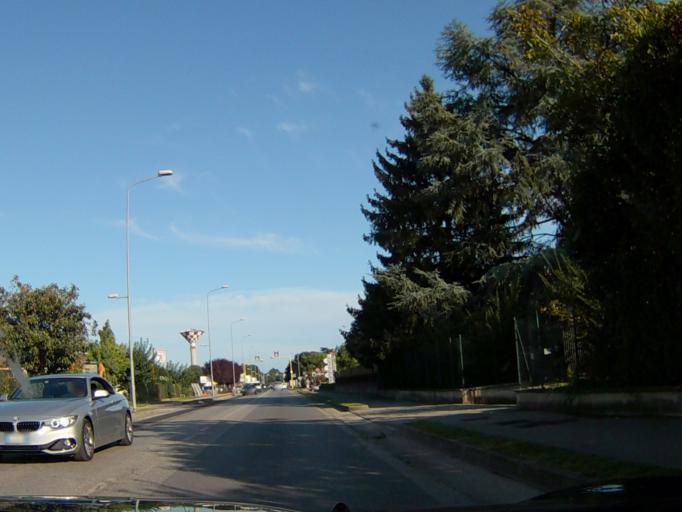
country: IT
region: Lombardy
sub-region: Provincia di Brescia
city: Molinetto
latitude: 45.4969
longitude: 10.3513
